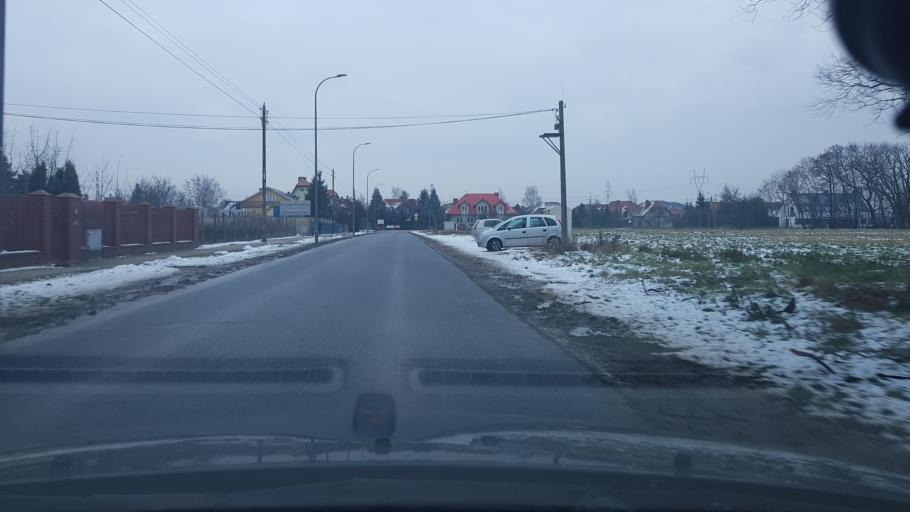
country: PL
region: Masovian Voivodeship
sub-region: Warszawa
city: Targowek
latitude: 52.3079
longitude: 21.0379
